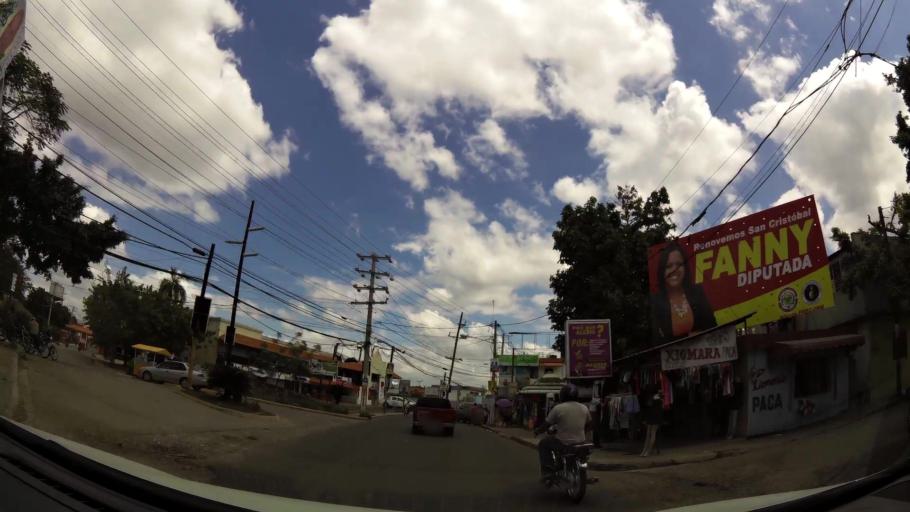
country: DO
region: San Cristobal
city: San Cristobal
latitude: 18.4145
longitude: -70.1043
